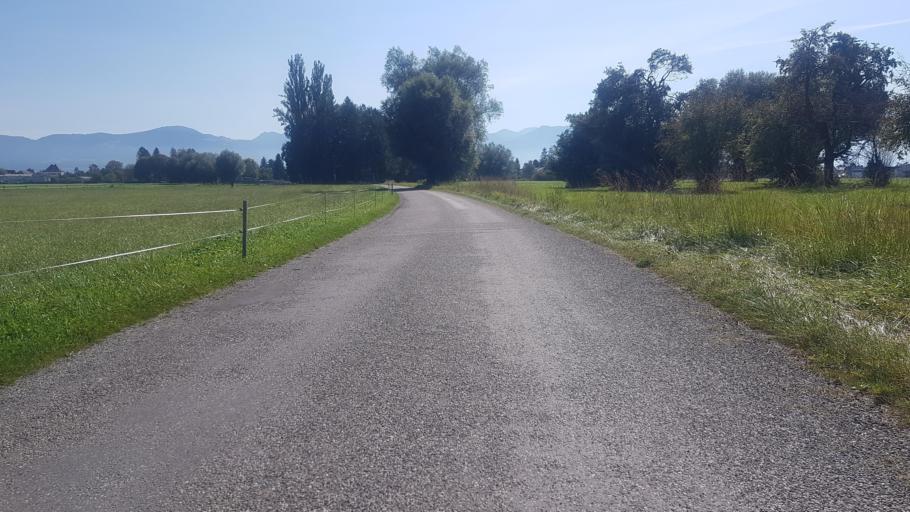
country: AT
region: Vorarlberg
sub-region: Politischer Bezirk Bregenz
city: Fussach
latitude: 47.4843
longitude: 9.6576
